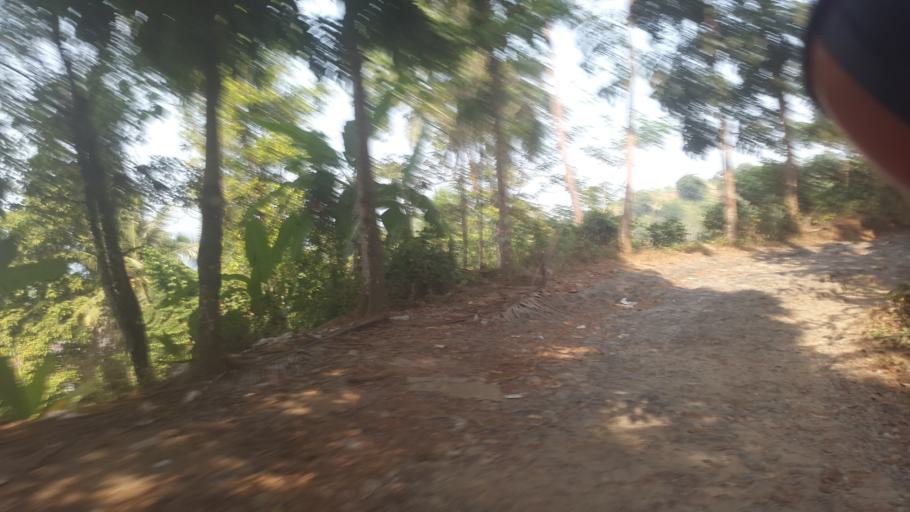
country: ID
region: West Java
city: Tugu
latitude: -6.9442
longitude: 106.4476
